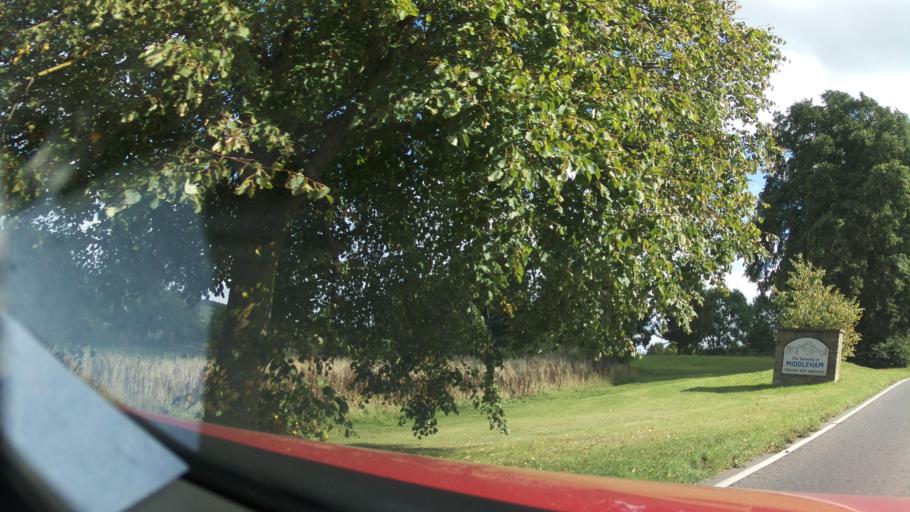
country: GB
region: England
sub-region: North Yorkshire
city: Leyburn
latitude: 54.2893
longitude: -1.8096
